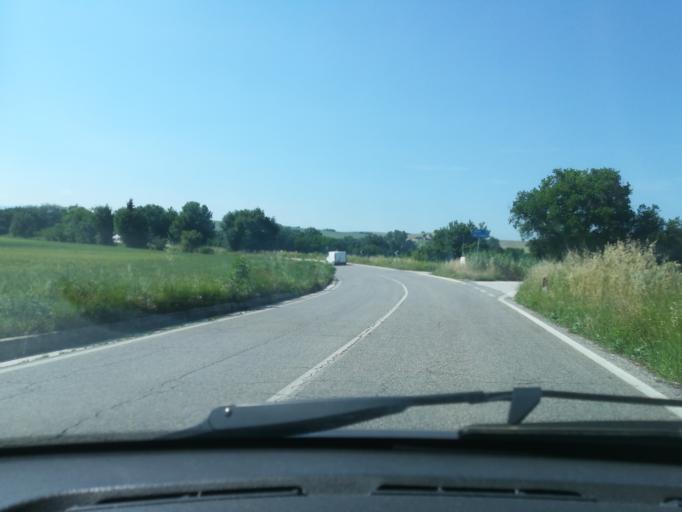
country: IT
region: The Marches
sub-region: Provincia di Macerata
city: Pollenza
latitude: 43.2930
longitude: 13.3788
